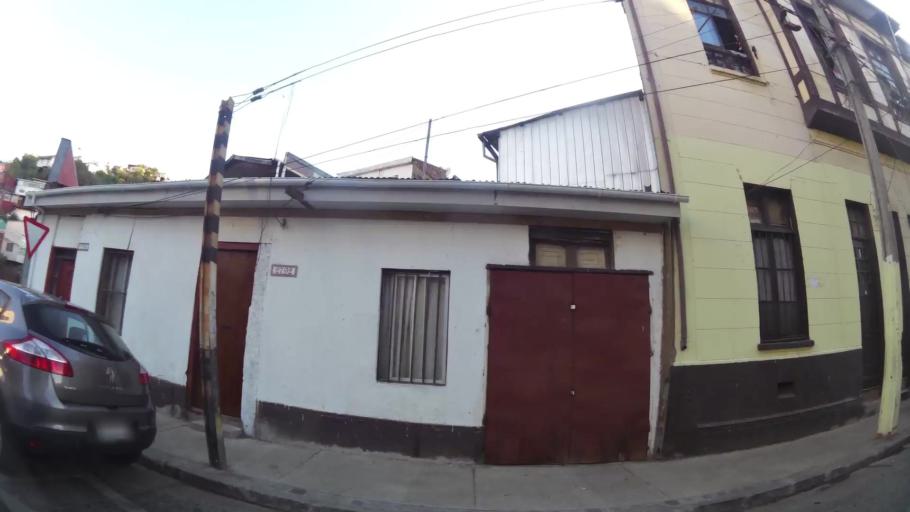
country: CL
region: Valparaiso
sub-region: Provincia de Valparaiso
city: Valparaiso
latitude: -33.0541
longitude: -71.6069
